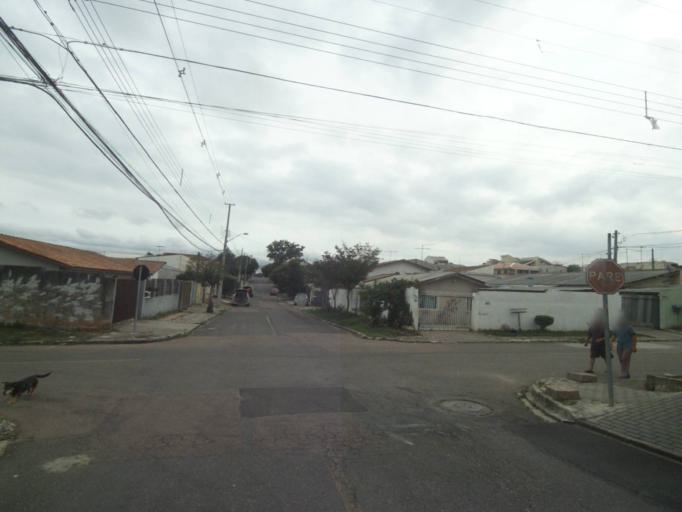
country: BR
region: Parana
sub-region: Sao Jose Dos Pinhais
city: Sao Jose dos Pinhais
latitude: -25.5514
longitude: -49.2681
